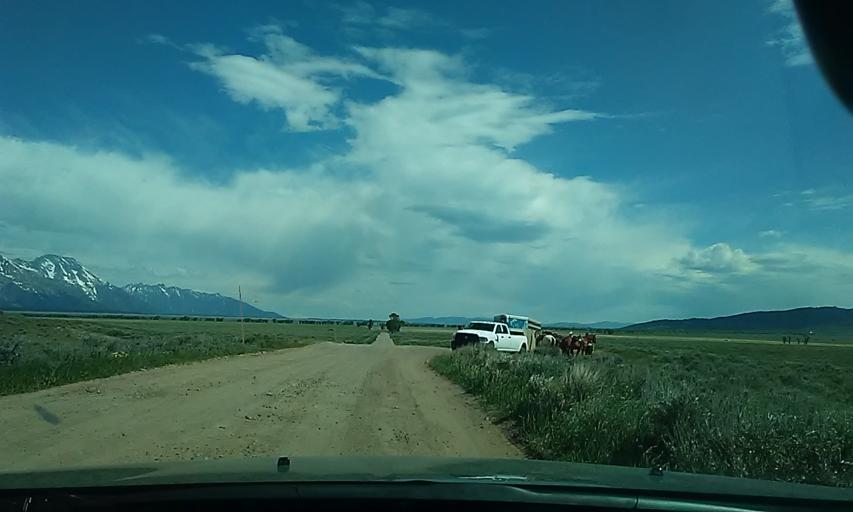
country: US
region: Wyoming
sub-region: Teton County
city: Jackson
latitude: 43.6258
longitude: -110.6642
